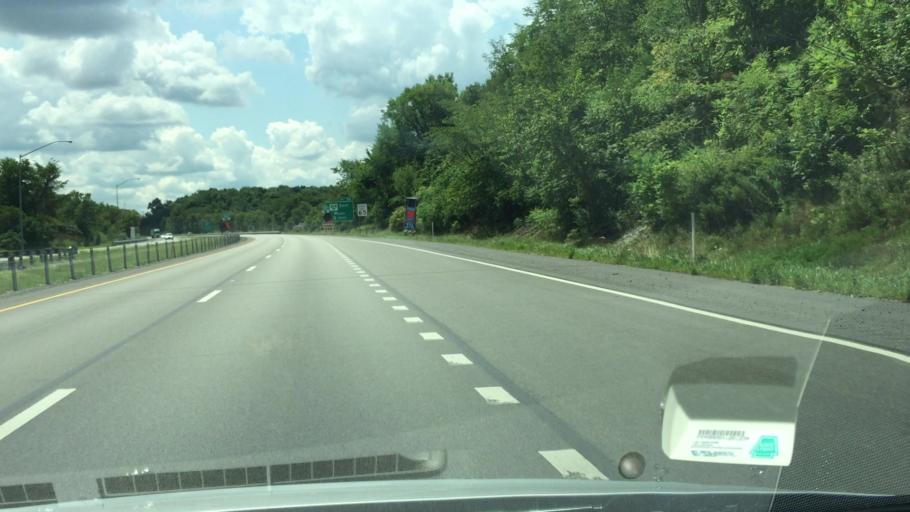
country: US
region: Pennsylvania
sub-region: Beaver County
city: Ambridge
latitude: 40.5567
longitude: -80.2792
